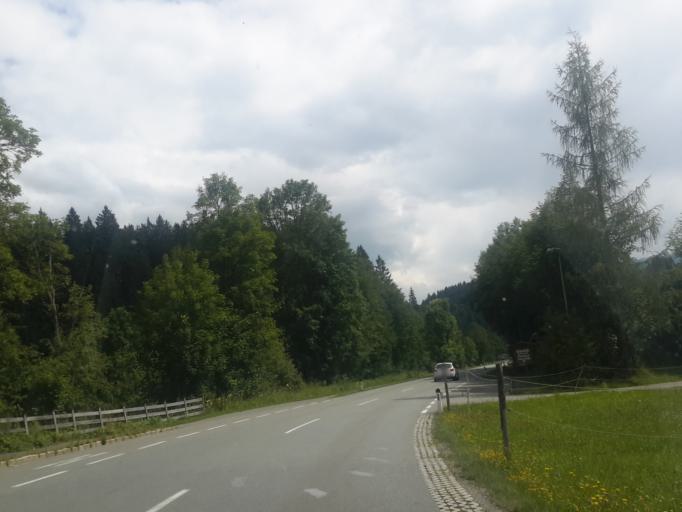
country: AT
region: Tyrol
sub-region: Politischer Bezirk Kitzbuhel
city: Oberndorf in Tirol
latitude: 47.5107
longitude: 12.3570
